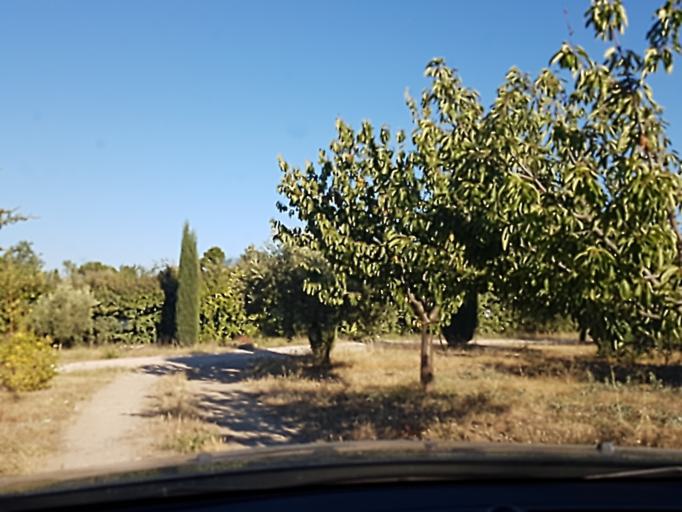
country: FR
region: Provence-Alpes-Cote d'Azur
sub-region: Departement des Bouches-du-Rhone
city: Eygalieres
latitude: 43.7664
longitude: 4.9282
